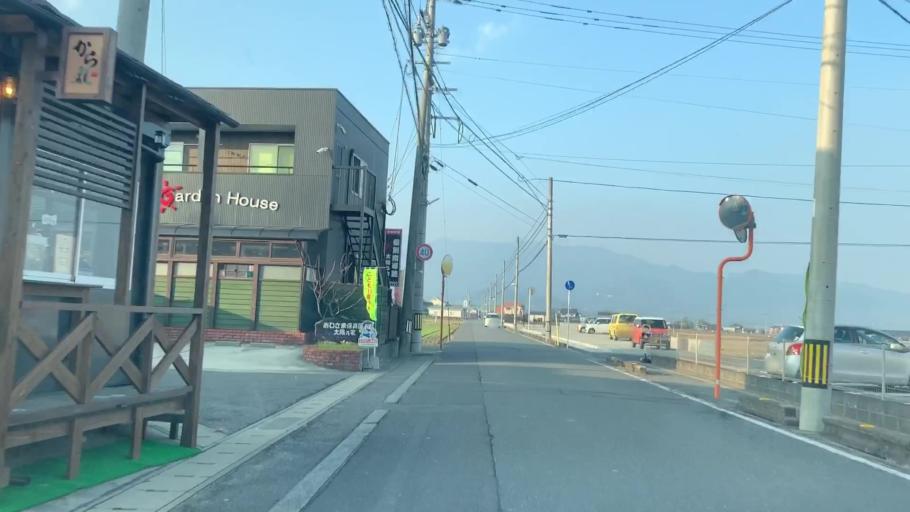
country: JP
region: Saga Prefecture
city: Saga-shi
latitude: 33.2731
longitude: 130.2283
